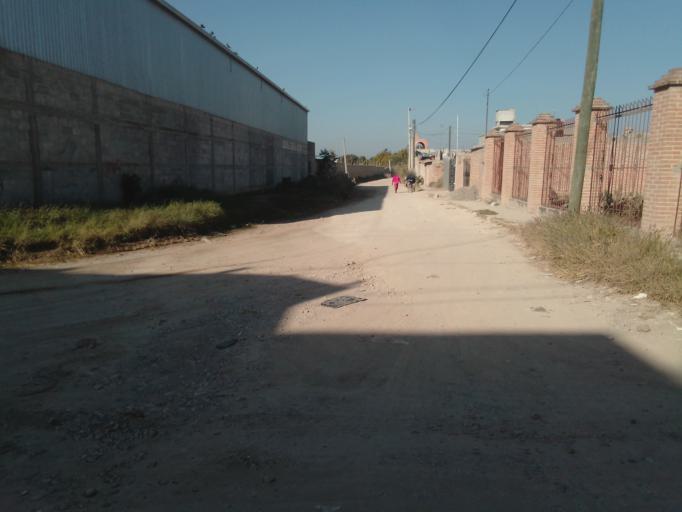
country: MX
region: Guanajuato
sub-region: San Luis de la Paz
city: San Ignacio
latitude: 21.2978
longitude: -100.5368
